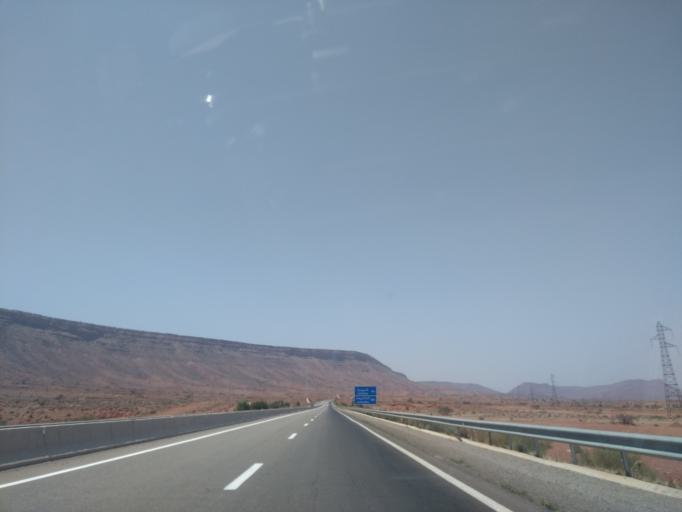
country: MA
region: Marrakech-Tensift-Al Haouz
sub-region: Chichaoua
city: Timezgadiouine
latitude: 30.9111
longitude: -9.0708
